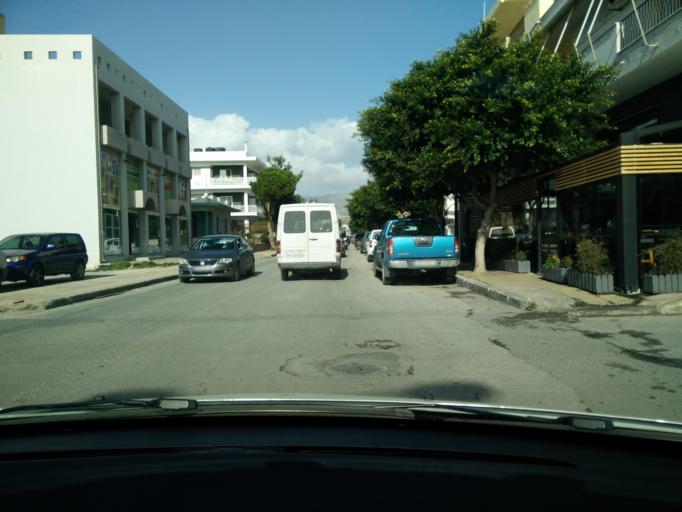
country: GR
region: Crete
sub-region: Nomos Lasithiou
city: Ierapetra
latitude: 35.0091
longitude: 25.7355
